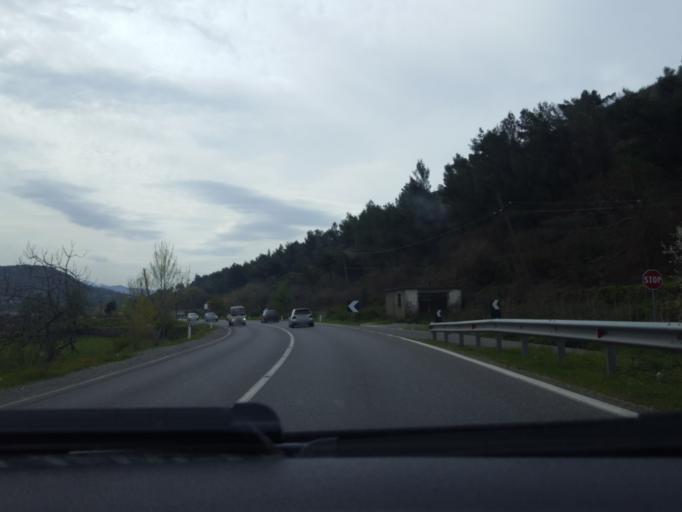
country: AL
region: Lezhe
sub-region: Rrethi i Lezhes
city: Balldreni i Ri
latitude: 41.8014
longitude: 19.6303
